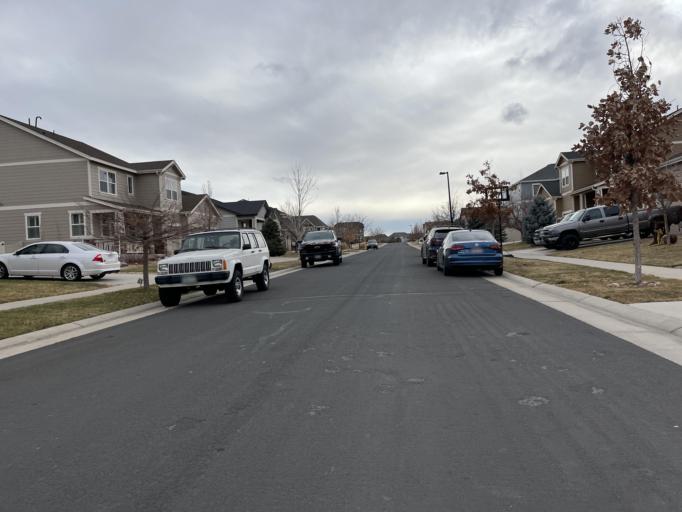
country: US
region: Colorado
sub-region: Douglas County
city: Parker
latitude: 39.4983
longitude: -104.7823
